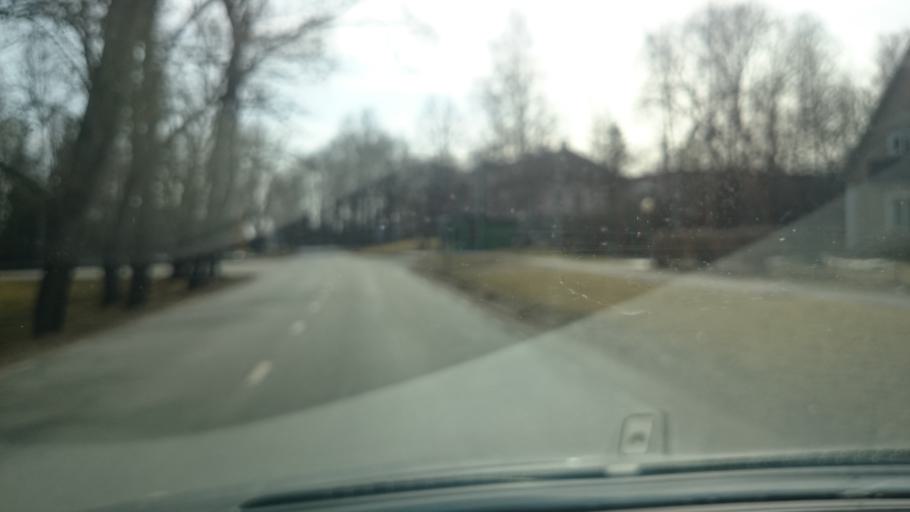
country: EE
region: Jaervamaa
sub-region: Tueri vald
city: Tueri
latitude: 58.8892
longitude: 25.4533
